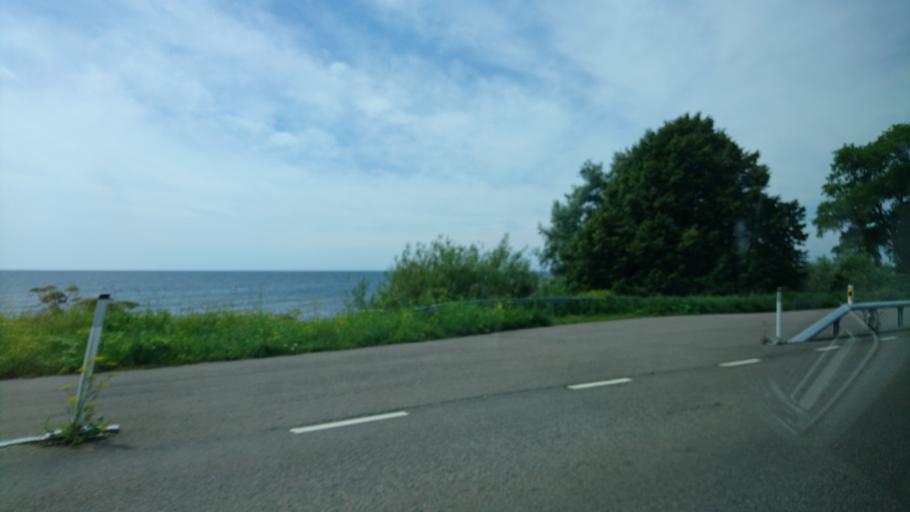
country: SE
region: Skane
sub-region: Skurups Kommun
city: Skivarp
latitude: 55.3860
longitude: 13.5522
